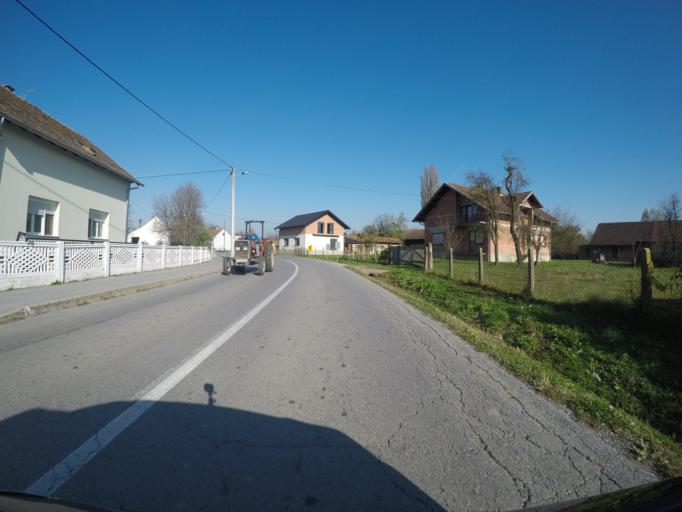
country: HR
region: Bjelovarsko-Bilogorska
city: Predavac
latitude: 45.9147
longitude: 16.7847
